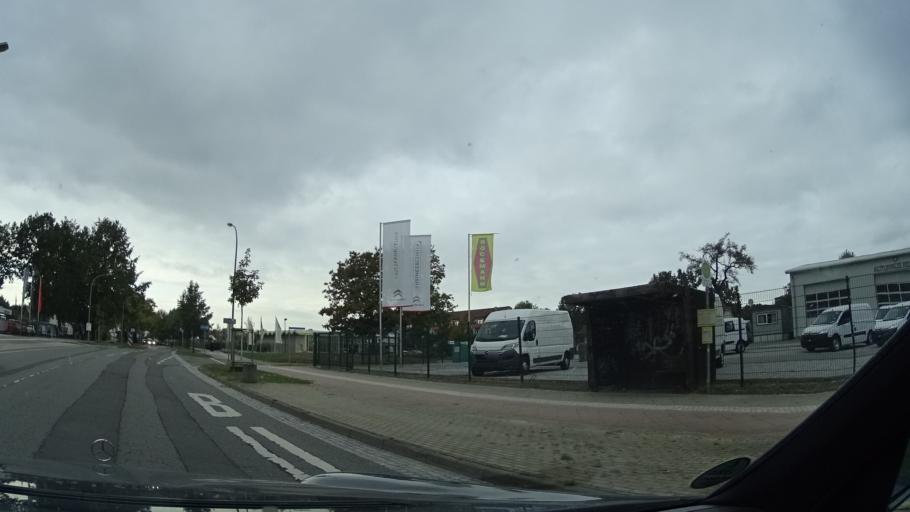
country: DE
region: Brandenburg
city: Neuruppin
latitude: 52.9386
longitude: 12.8162
